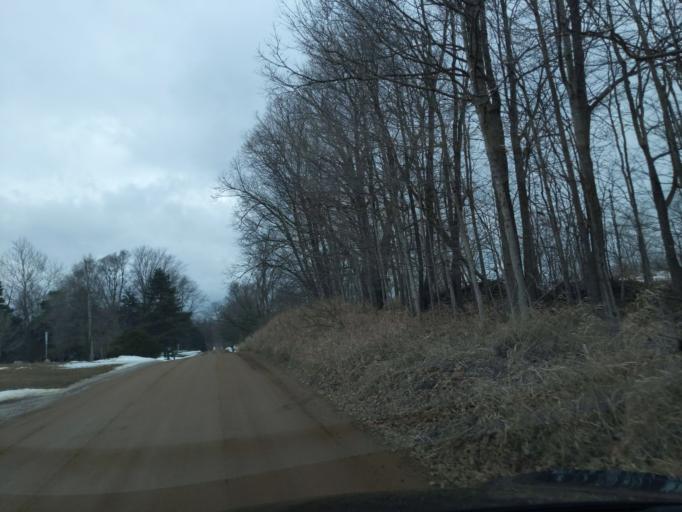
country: US
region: Michigan
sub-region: Eaton County
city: Eaton Rapids
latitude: 42.5386
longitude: -84.6106
